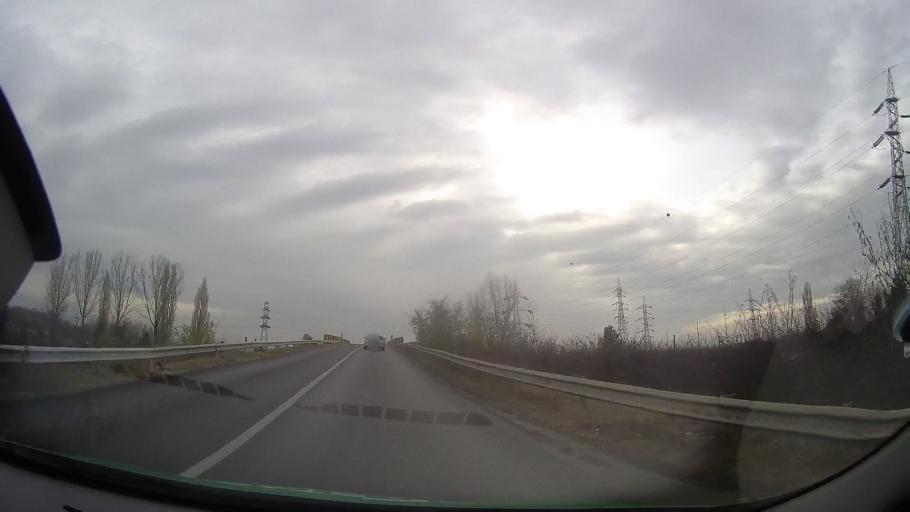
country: RO
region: Prahova
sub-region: Comuna Berceni
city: Berceni
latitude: 44.9418
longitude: 26.1013
